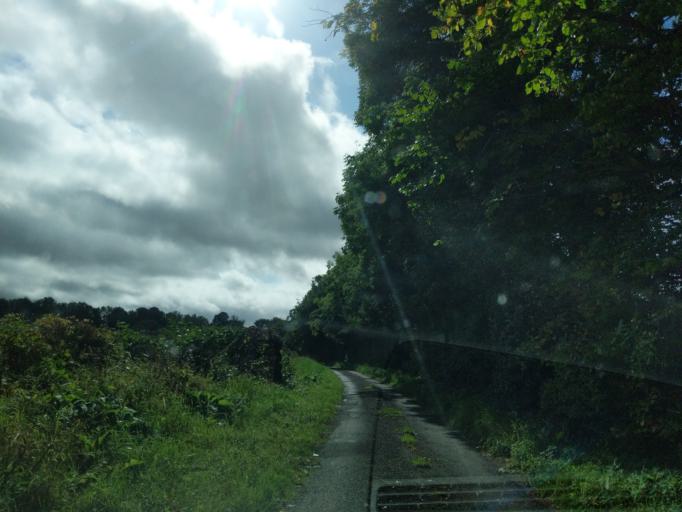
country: GB
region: Scotland
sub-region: The Scottish Borders
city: Kelso
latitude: 55.5698
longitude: -2.4718
